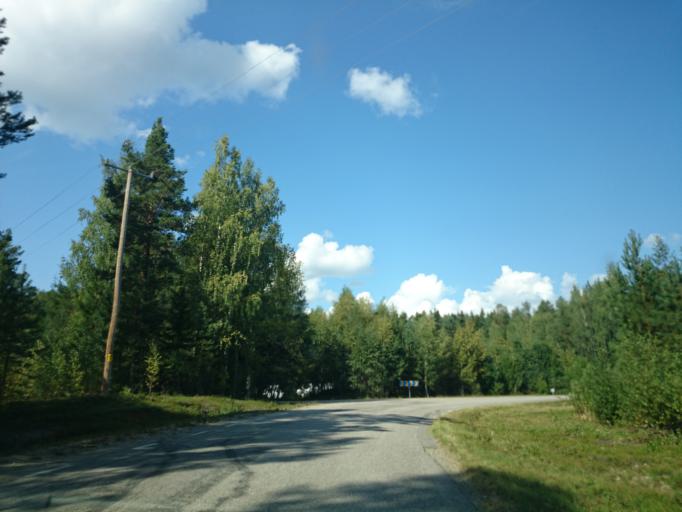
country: SE
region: Gaevleborg
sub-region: Ljusdals Kommun
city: Jaervsoe
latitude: 61.7759
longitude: 16.2120
